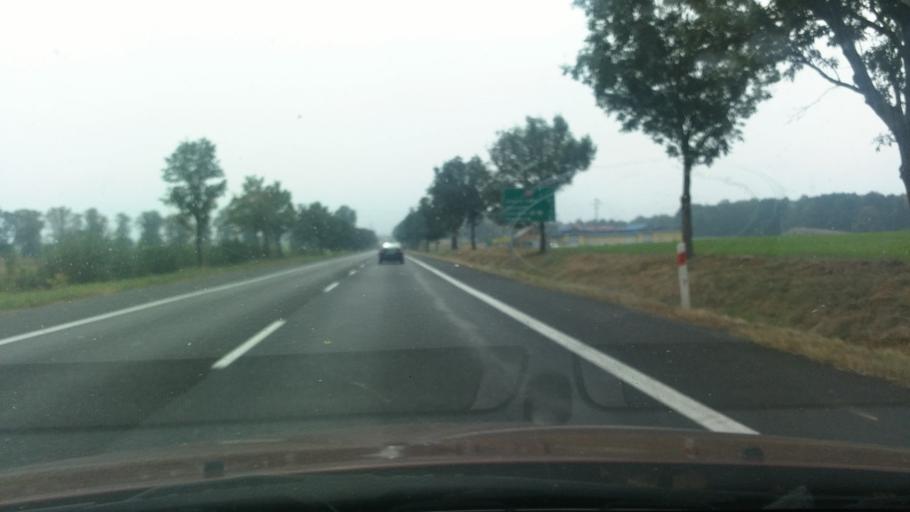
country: PL
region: Lower Silesian Voivodeship
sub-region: Powiat zgorzelecki
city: Lagow
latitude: 51.1664
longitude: 15.0297
